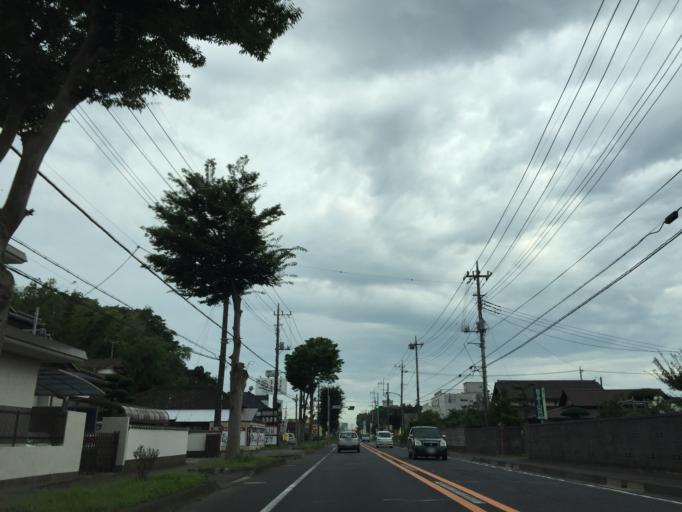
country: JP
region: Ibaraki
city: Naka
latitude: 36.0228
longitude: 140.1603
